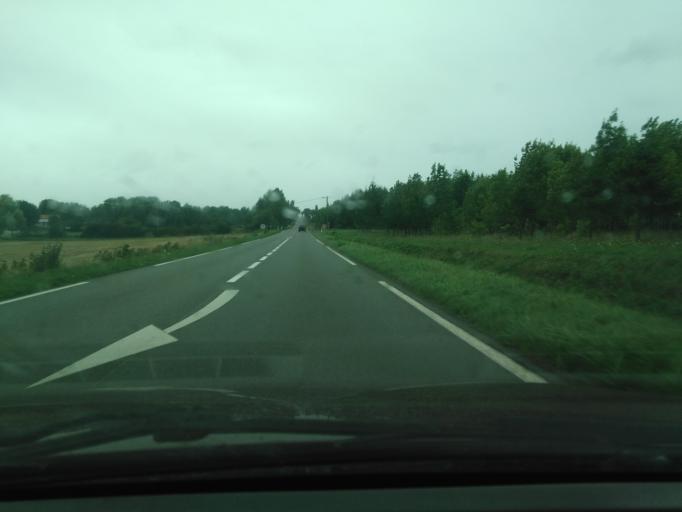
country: FR
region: Pays de la Loire
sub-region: Departement de la Vendee
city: Sainte-Hermine
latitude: 46.5653
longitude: -1.0797
